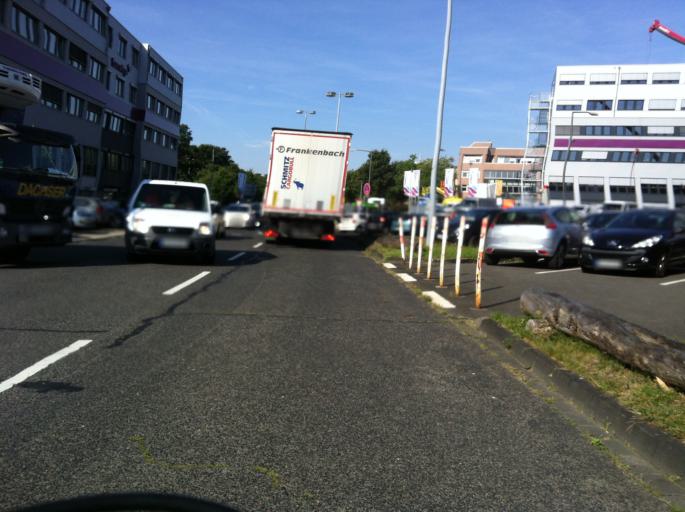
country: DE
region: North Rhine-Westphalia
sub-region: Regierungsbezirk Koln
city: Wahn-Heide
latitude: 50.8797
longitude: 7.1128
